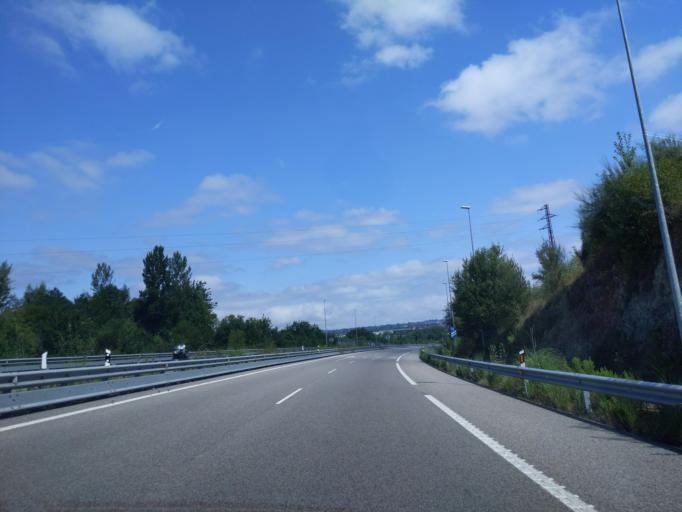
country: ES
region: Asturias
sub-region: Province of Asturias
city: Norena
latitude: 43.3669
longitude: -5.7251
